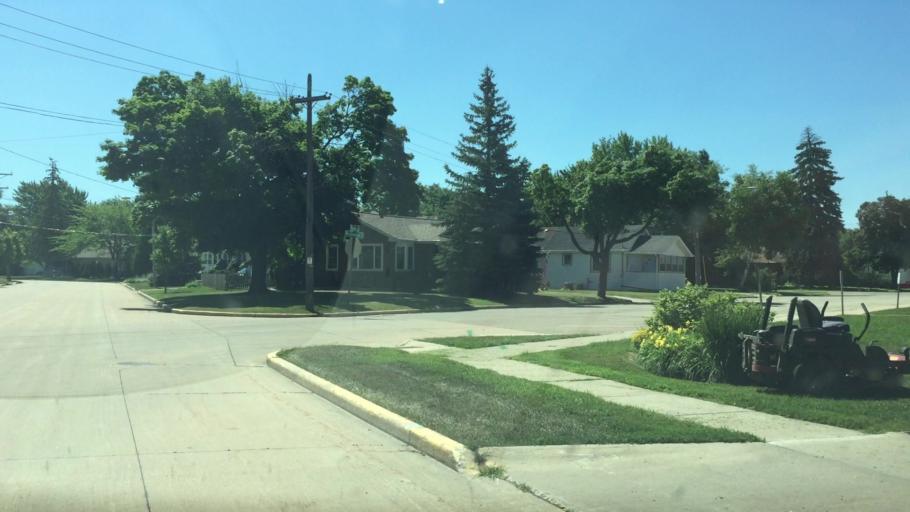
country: US
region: Wisconsin
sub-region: Winnebago County
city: Neenah
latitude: 44.1793
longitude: -88.4551
